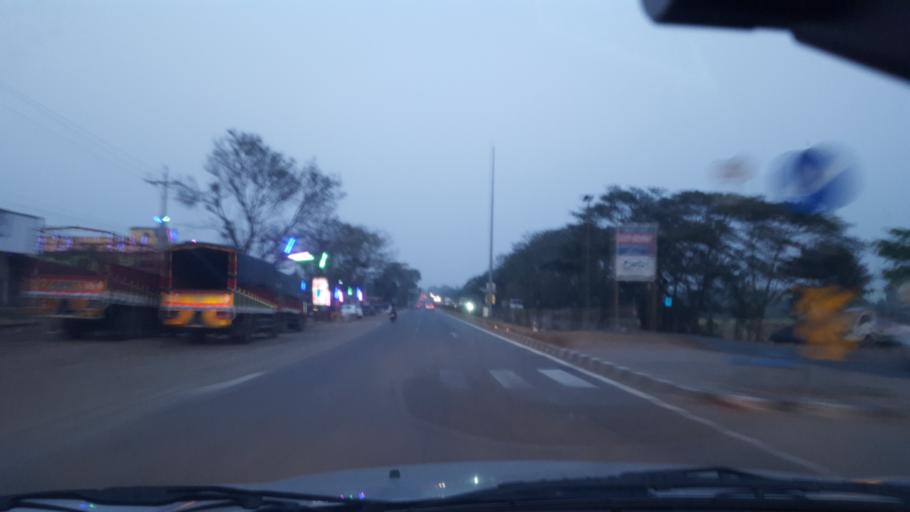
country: IN
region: Andhra Pradesh
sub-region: East Godavari
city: Rajahmundry
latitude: 17.0350
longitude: 81.8280
